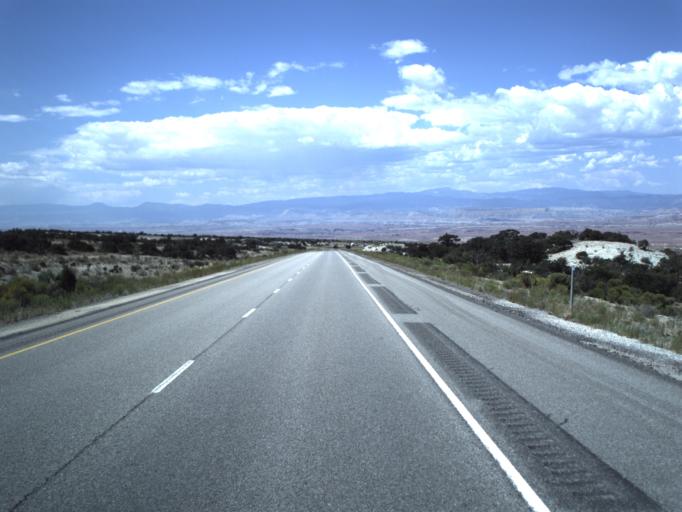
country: US
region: Utah
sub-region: Emery County
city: Ferron
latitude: 38.8456
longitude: -110.9456
